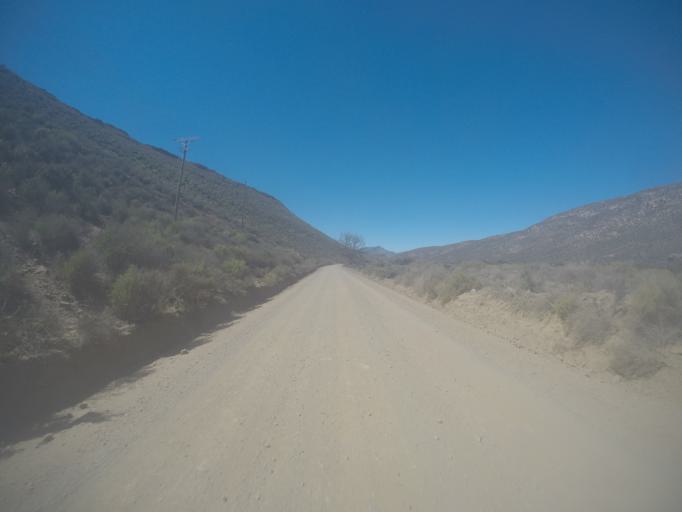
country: ZA
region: Western Cape
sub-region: West Coast District Municipality
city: Clanwilliam
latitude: -32.5070
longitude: 19.3417
